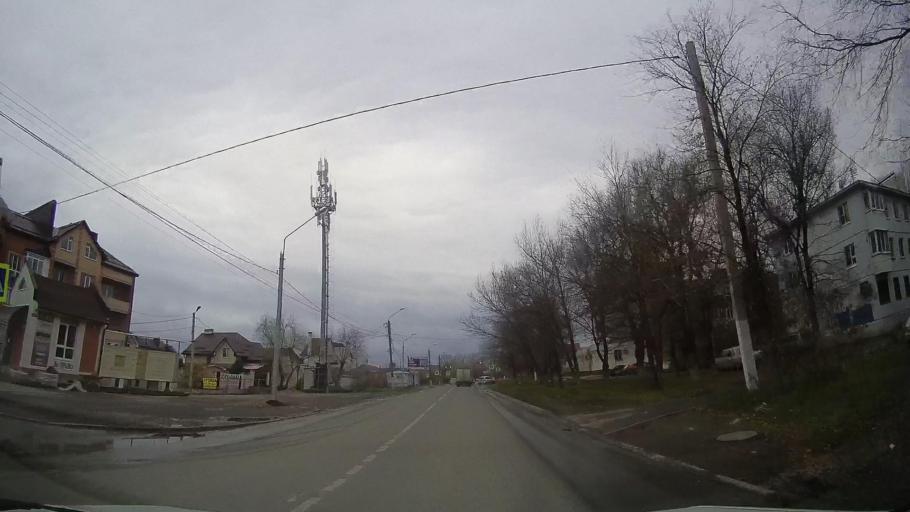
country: RU
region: Rostov
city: Bataysk
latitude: 47.1304
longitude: 39.7431
